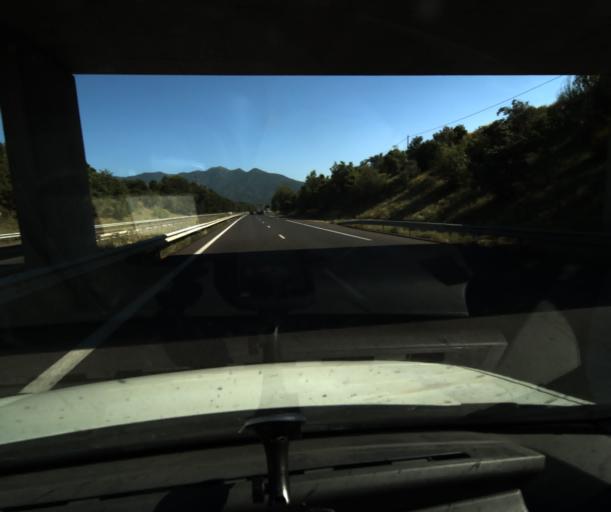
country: FR
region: Languedoc-Roussillon
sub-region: Departement des Pyrenees-Orientales
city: Banyuls-dels-Aspres
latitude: 42.5569
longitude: 2.8476
